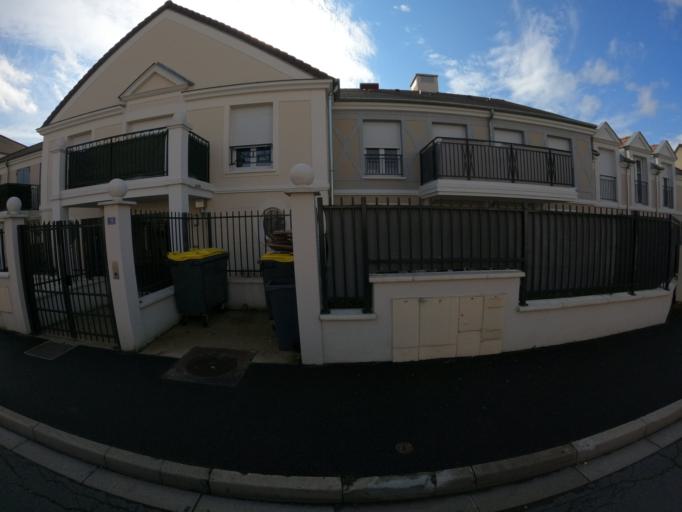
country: FR
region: Ile-de-France
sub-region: Departement de Seine-et-Marne
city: Vaires-sur-Marne
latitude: 48.8769
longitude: 2.6348
